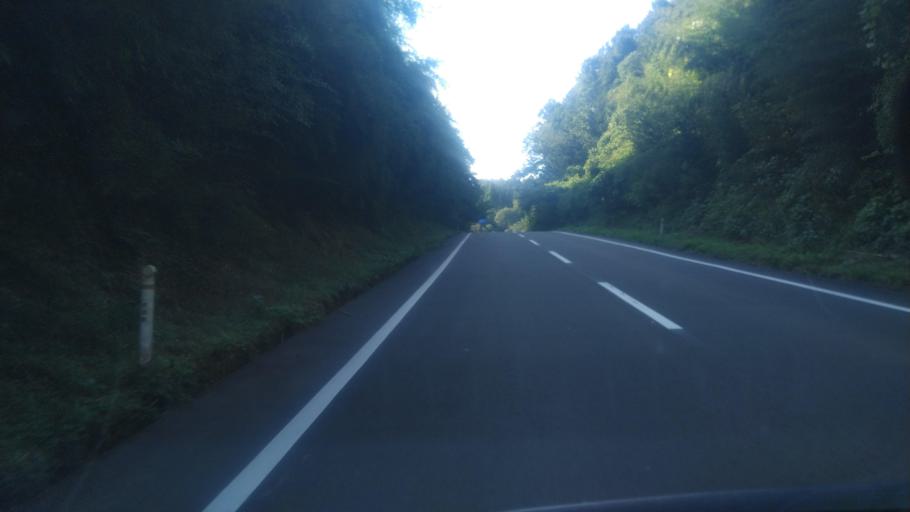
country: JP
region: Miyagi
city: Okawara
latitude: 38.0987
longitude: 140.7079
